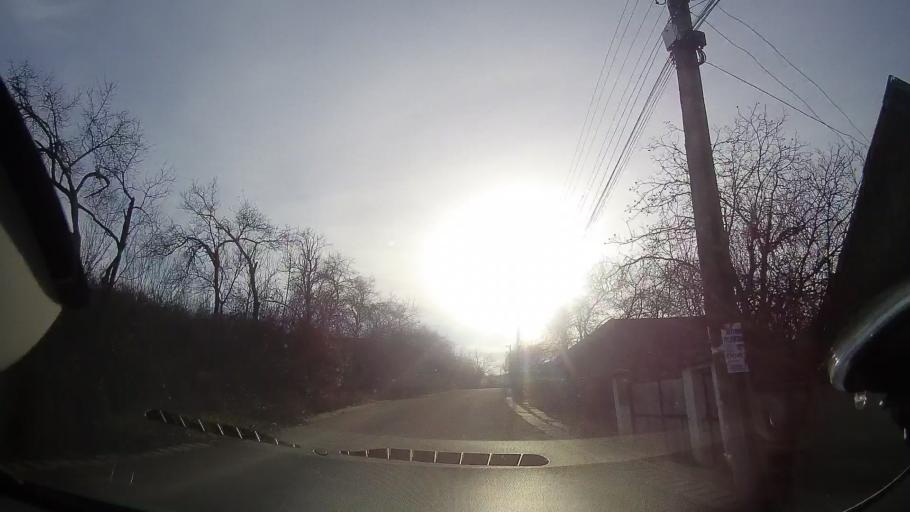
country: RO
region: Bihor
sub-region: Comuna Sarbi
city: Burzuc
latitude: 47.1430
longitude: 22.1853
